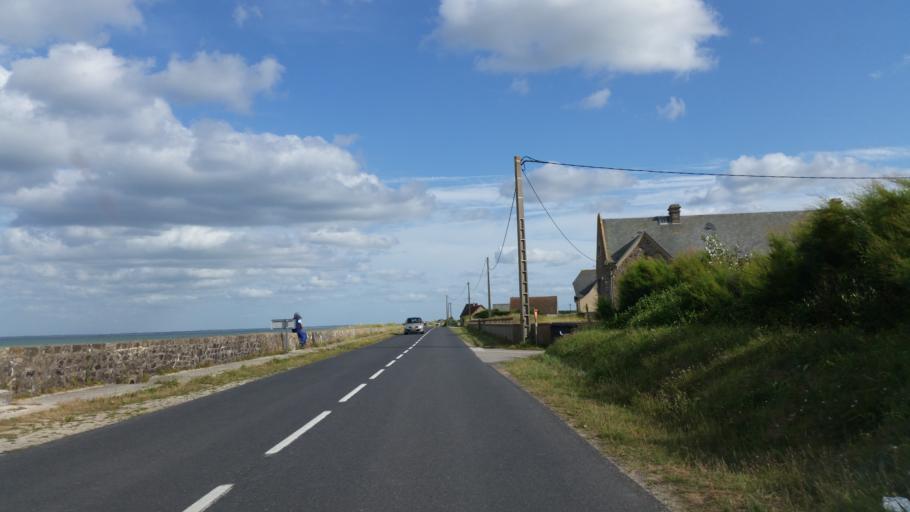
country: FR
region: Lower Normandy
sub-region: Departement de la Manche
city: Sainte-Mere-Eglise
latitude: 49.4560
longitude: -1.2234
